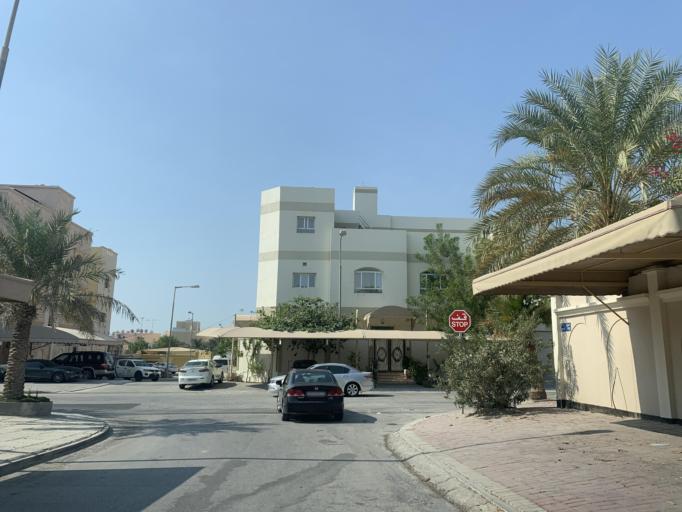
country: BH
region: Central Governorate
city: Madinat Hamad
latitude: 26.1144
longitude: 50.5005
